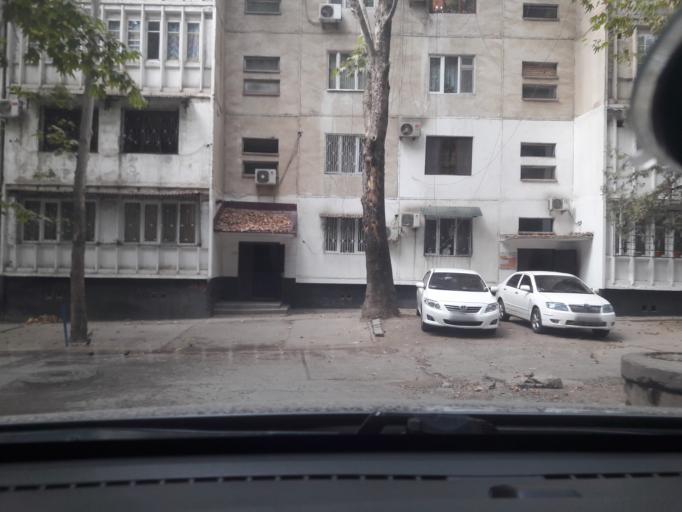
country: TJ
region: Dushanbe
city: Dushanbe
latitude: 38.5884
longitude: 68.7502
